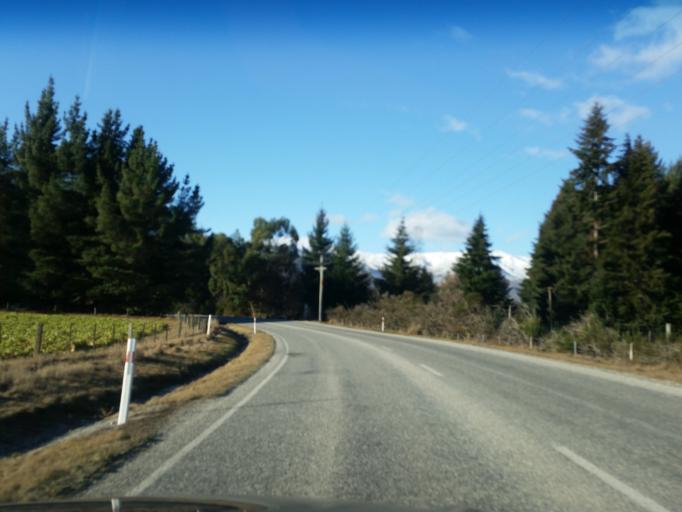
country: NZ
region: Otago
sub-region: Queenstown-Lakes District
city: Arrowtown
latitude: -44.9558
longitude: 168.7408
